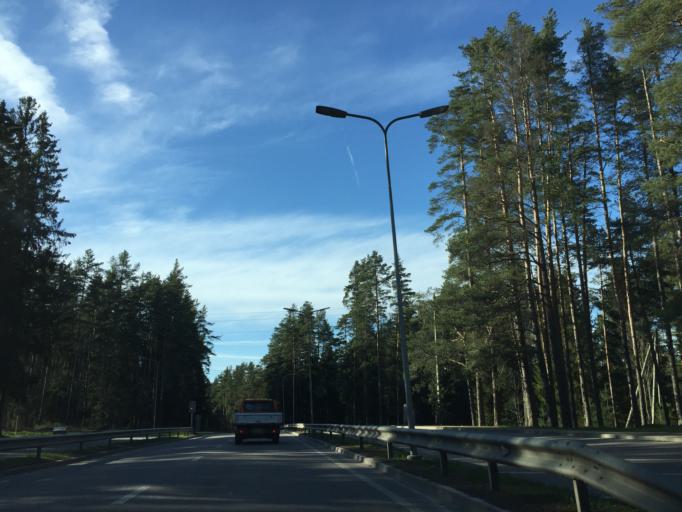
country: LV
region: Valkas Rajons
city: Valka
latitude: 57.7831
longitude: 26.0032
